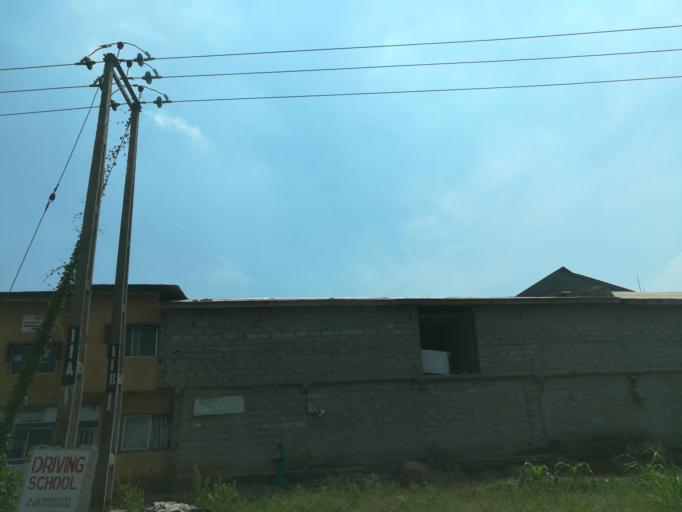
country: NG
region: Lagos
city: Ikorodu
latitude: 6.6448
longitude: 3.4798
